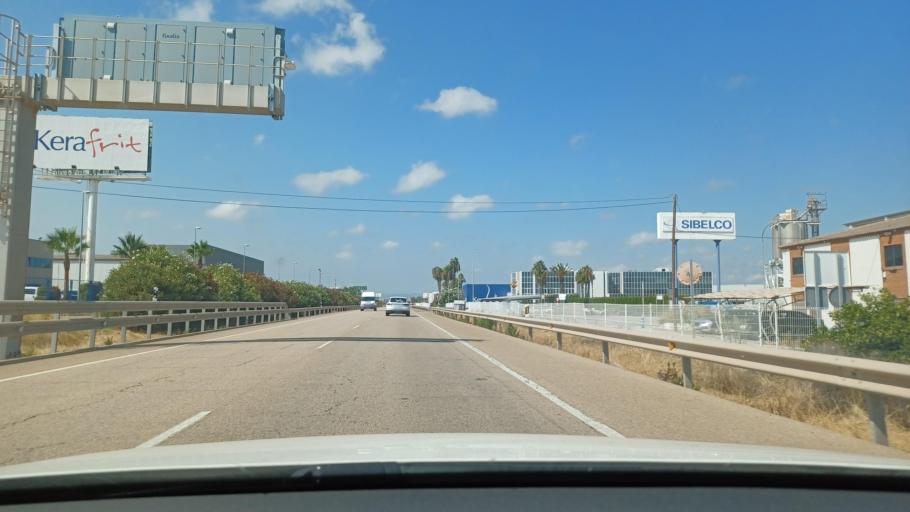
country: ES
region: Valencia
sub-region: Provincia de Castello
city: Moncofar
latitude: 39.8213
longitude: -0.1660
